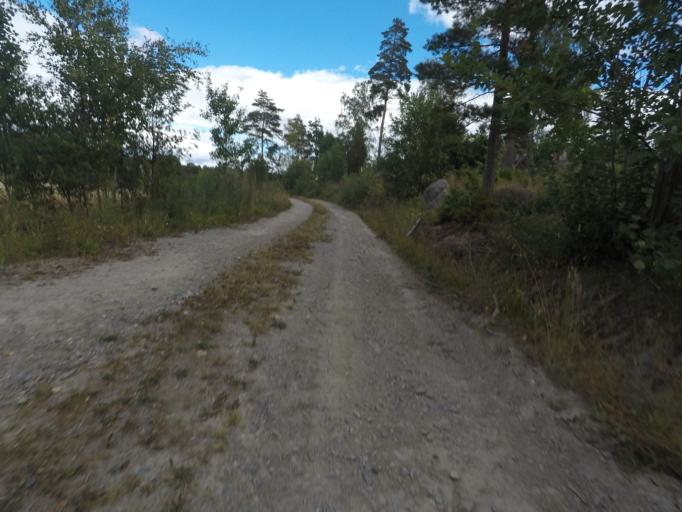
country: SE
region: Soedermanland
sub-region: Eskilstuna Kommun
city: Kvicksund
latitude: 59.4330
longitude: 16.2922
